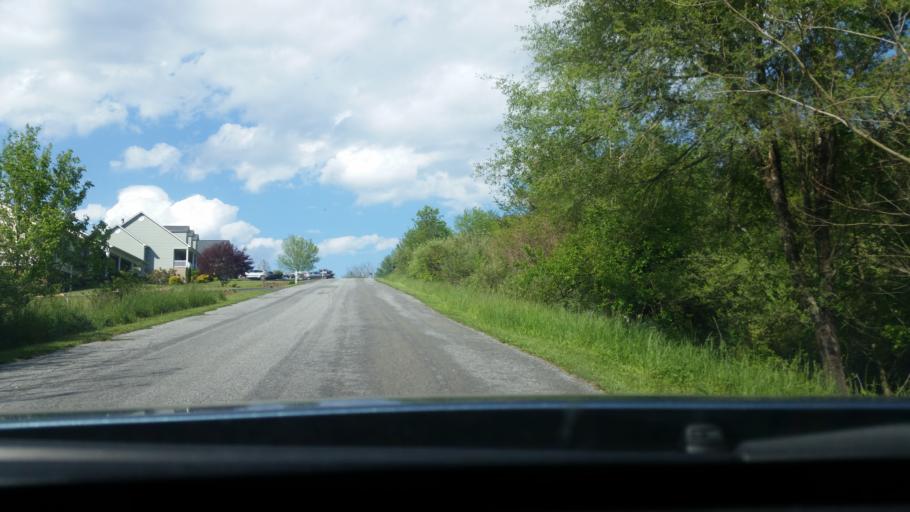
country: US
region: Virginia
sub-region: Giles County
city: Pembroke
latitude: 37.3108
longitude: -80.6311
